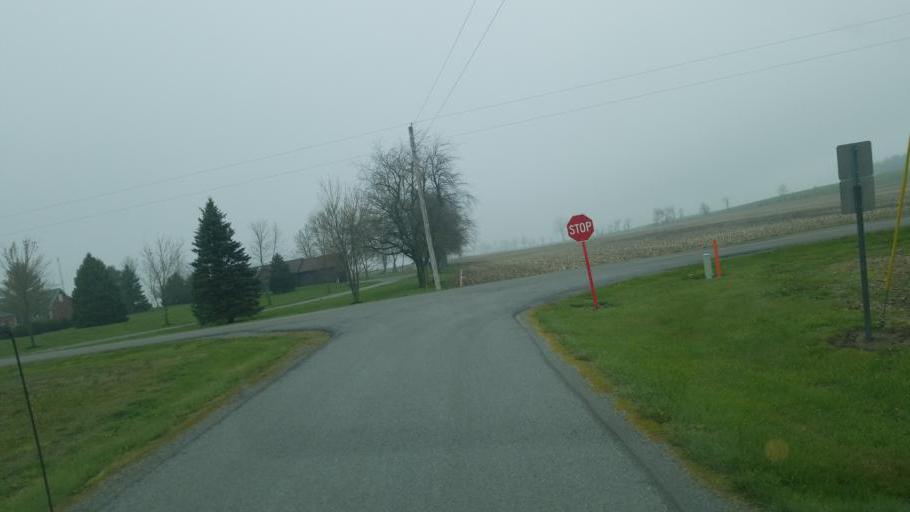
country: US
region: Ohio
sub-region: Logan County
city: Bellefontaine
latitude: 40.4063
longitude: -83.8265
